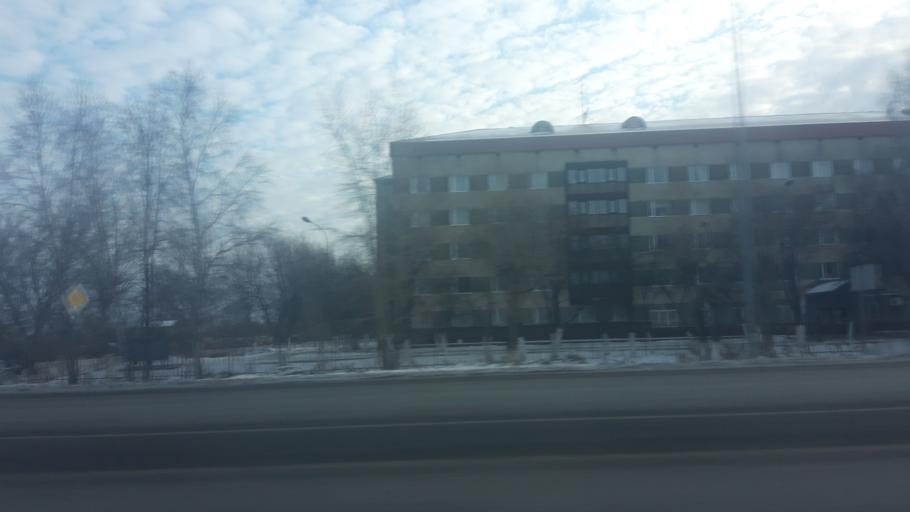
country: RU
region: Tjumen
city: Moskovskiy
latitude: 57.1846
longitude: 65.3543
